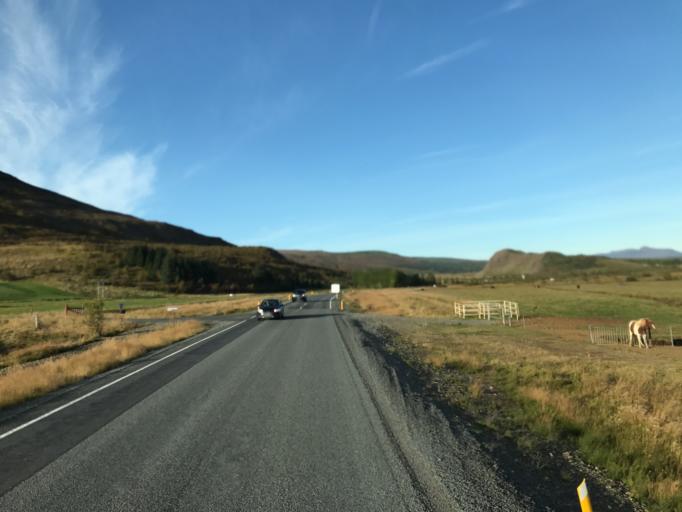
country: IS
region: South
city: Selfoss
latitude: 64.2999
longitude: -20.3312
